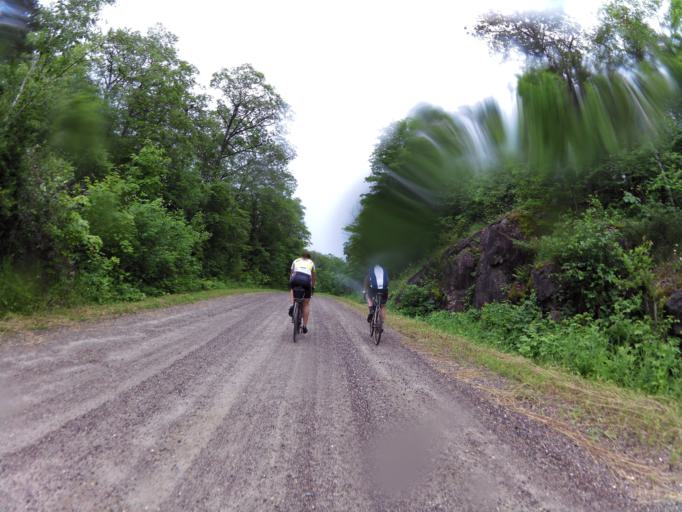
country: CA
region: Ontario
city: Renfrew
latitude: 45.1034
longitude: -76.6054
